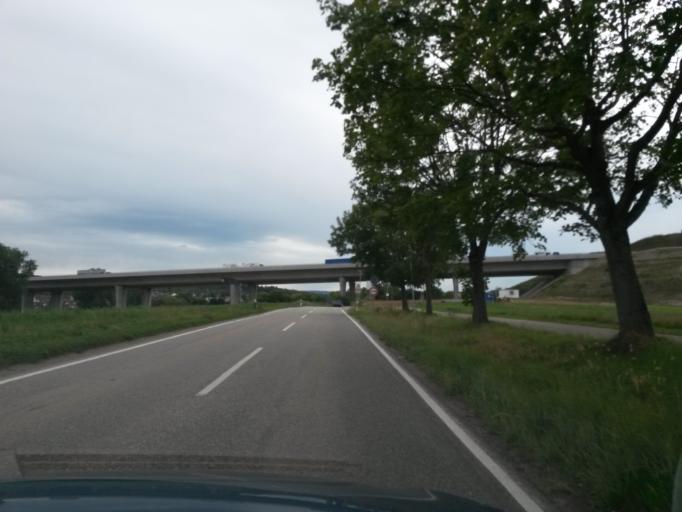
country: DE
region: Baden-Wuerttemberg
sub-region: Karlsruhe Region
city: Konigsbach-Stein
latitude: 48.9360
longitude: 8.5717
